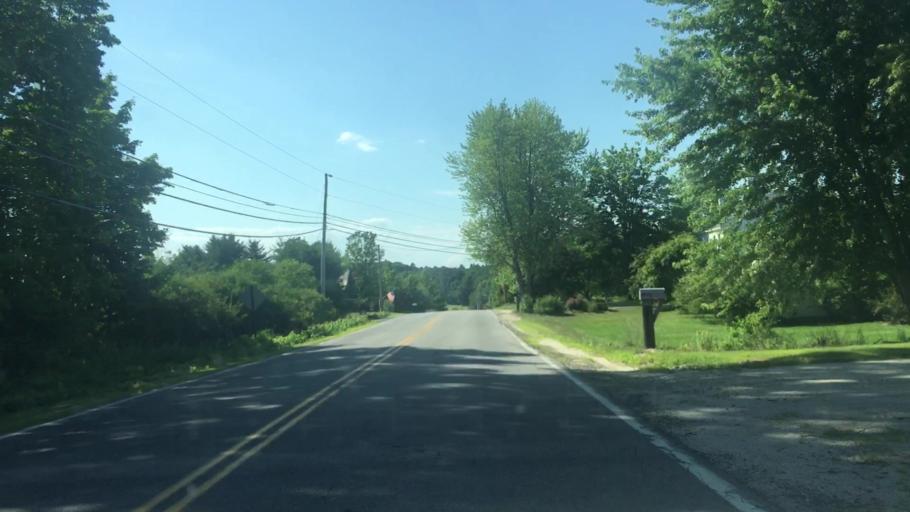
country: US
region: Maine
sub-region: York County
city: Buxton
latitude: 43.6269
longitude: -70.5511
